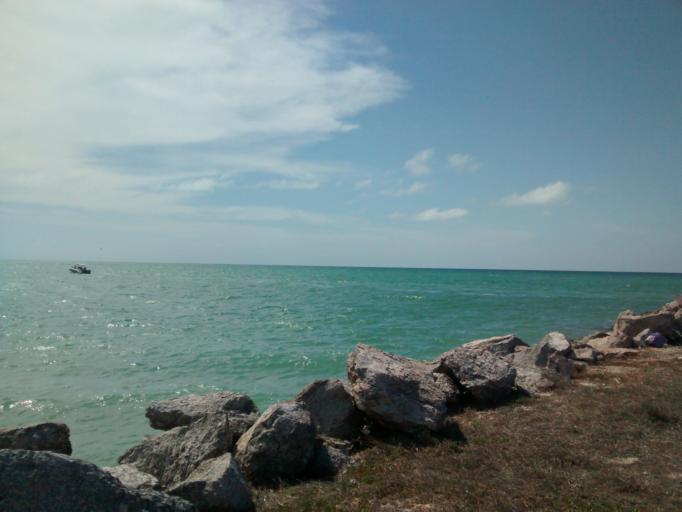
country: MX
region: Yucatan
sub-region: Progreso
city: Chelem
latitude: 21.2806
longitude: -89.7037
